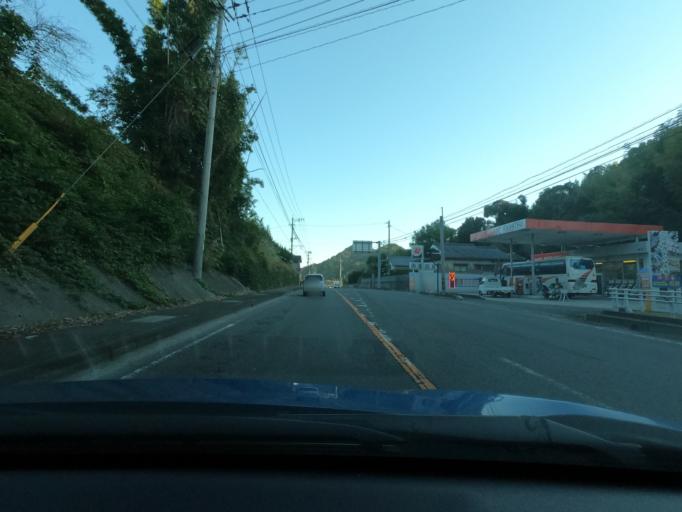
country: JP
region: Kagoshima
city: Satsumasendai
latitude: 31.8578
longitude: 130.2319
